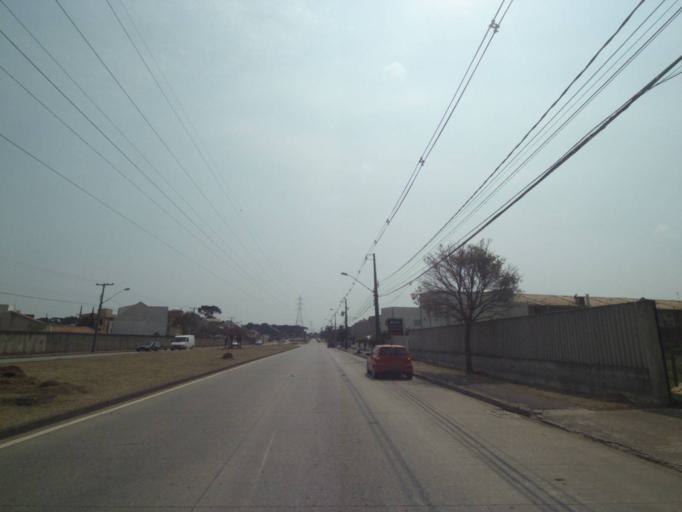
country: BR
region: Parana
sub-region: Sao Jose Dos Pinhais
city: Sao Jose dos Pinhais
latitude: -25.4977
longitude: -49.2093
